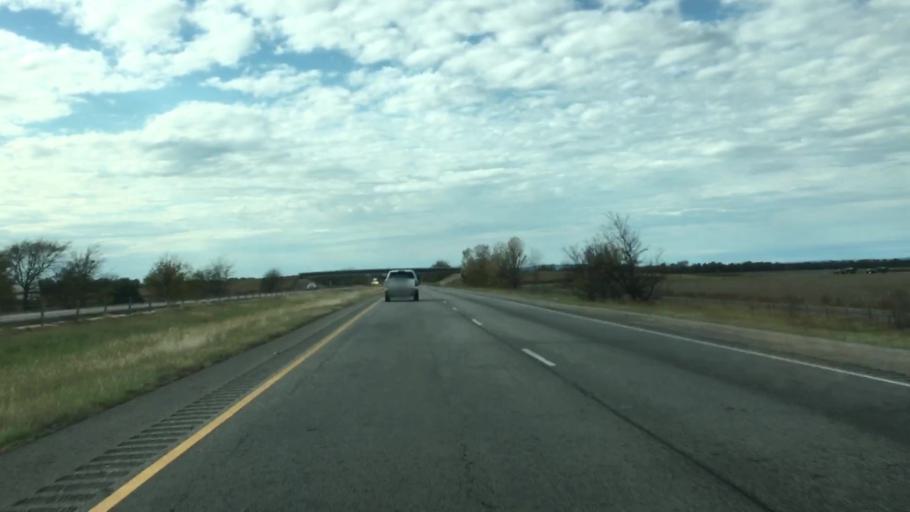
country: US
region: Arkansas
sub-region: Conway County
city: Morrilton
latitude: 35.1900
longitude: -92.7843
